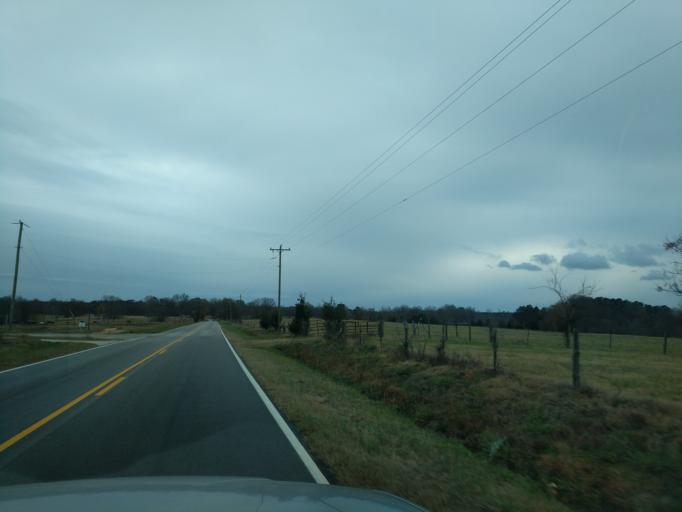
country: US
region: South Carolina
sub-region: Laurens County
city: Laurens
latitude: 34.3538
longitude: -81.9907
